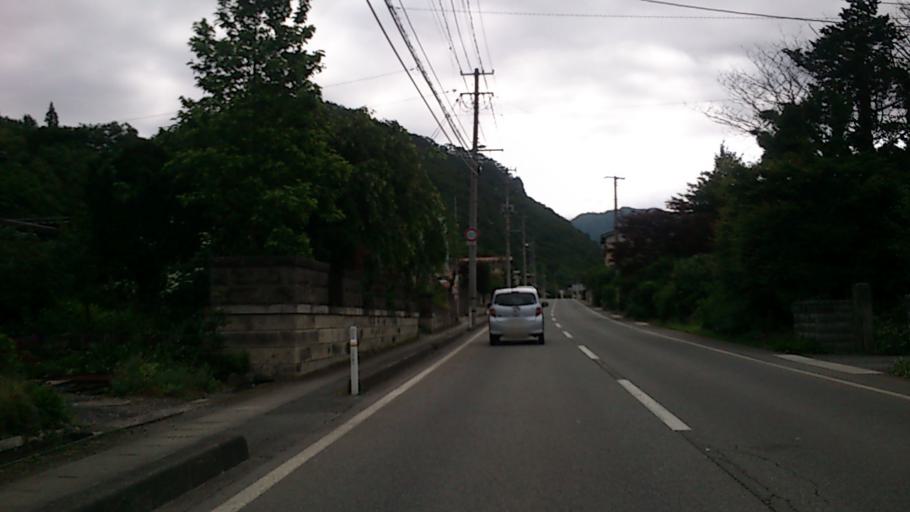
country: JP
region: Yamagata
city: Tendo
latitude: 38.3118
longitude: 140.4192
